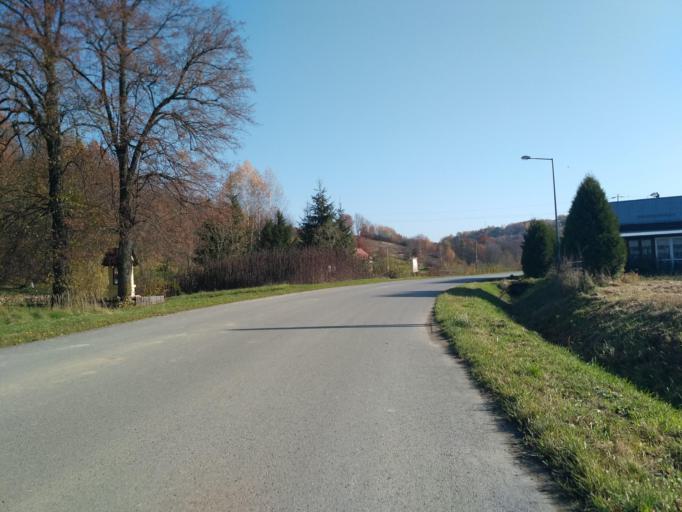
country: PL
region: Subcarpathian Voivodeship
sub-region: Powiat brzozowski
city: Nozdrzec
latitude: 49.7952
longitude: 22.1787
